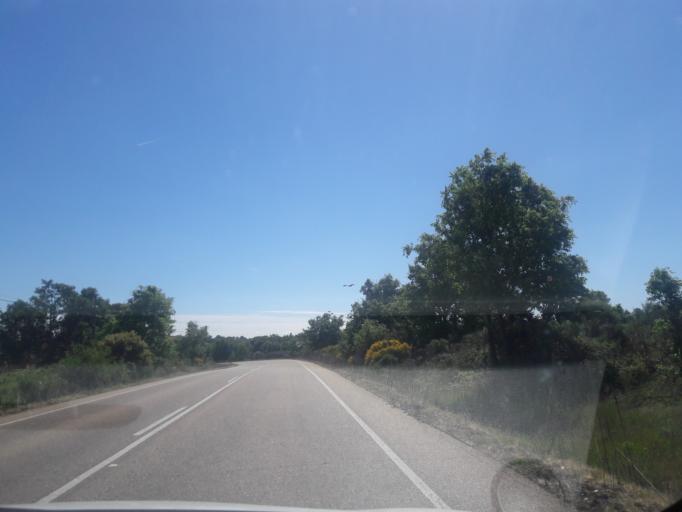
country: ES
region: Castille and Leon
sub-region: Provincia de Salamanca
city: Encinasola de los Comendadores
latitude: 40.9939
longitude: -6.5386
